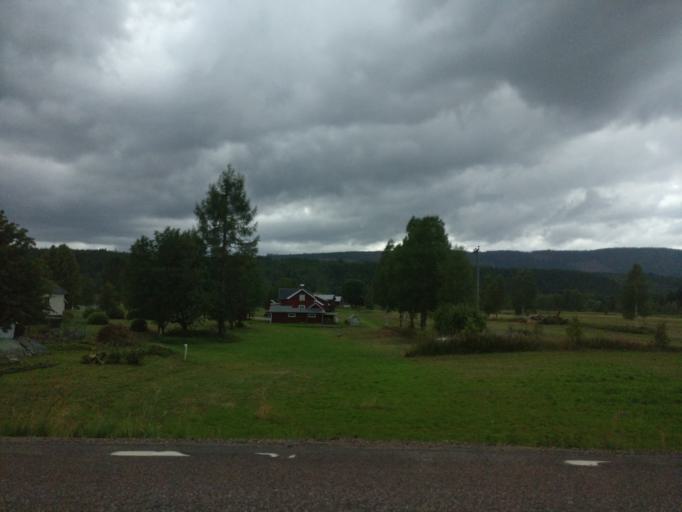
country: SE
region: Vaermland
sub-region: Torsby Kommun
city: Torsby
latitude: 60.6338
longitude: 13.0185
